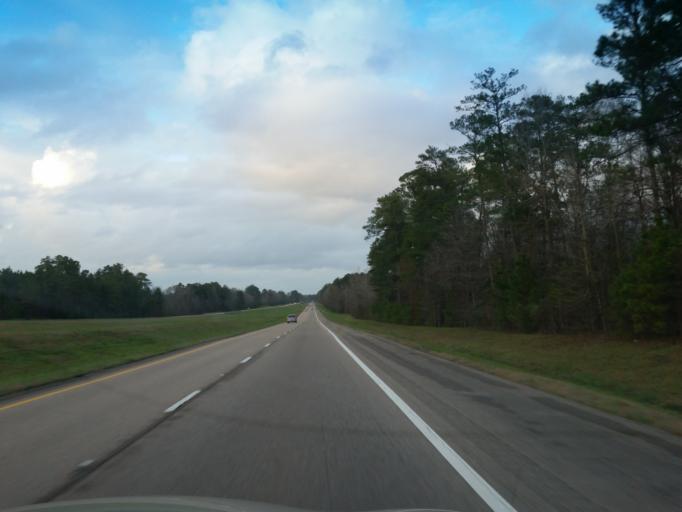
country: US
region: Mississippi
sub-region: Clarke County
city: Stonewall
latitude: 32.0214
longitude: -88.9228
